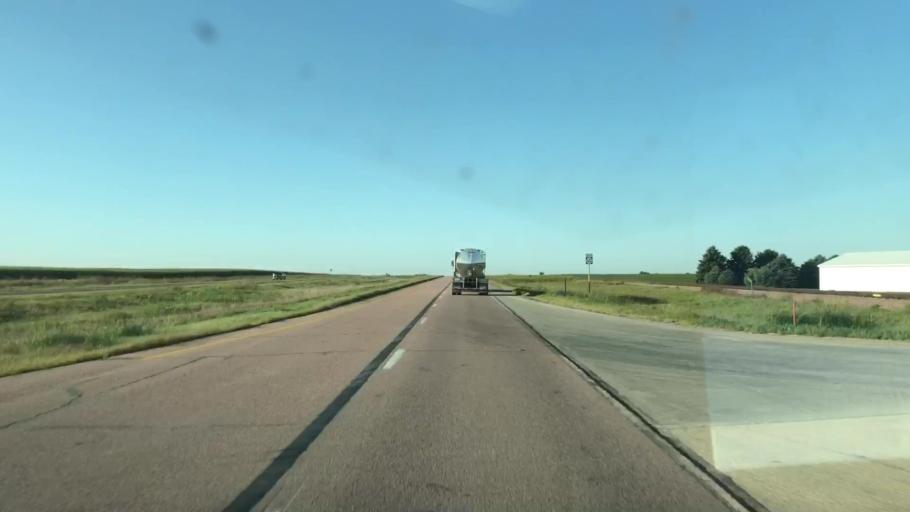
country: US
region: Iowa
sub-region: O'Brien County
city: Sheldon
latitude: 43.2724
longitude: -95.8064
